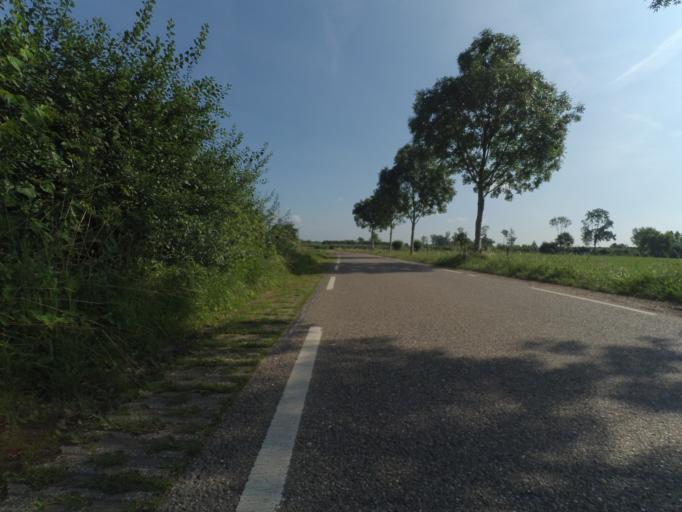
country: NL
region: Utrecht
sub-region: Gemeente Wijk bij Duurstede
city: Wijk bij Duurstede
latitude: 51.9928
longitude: 5.3344
